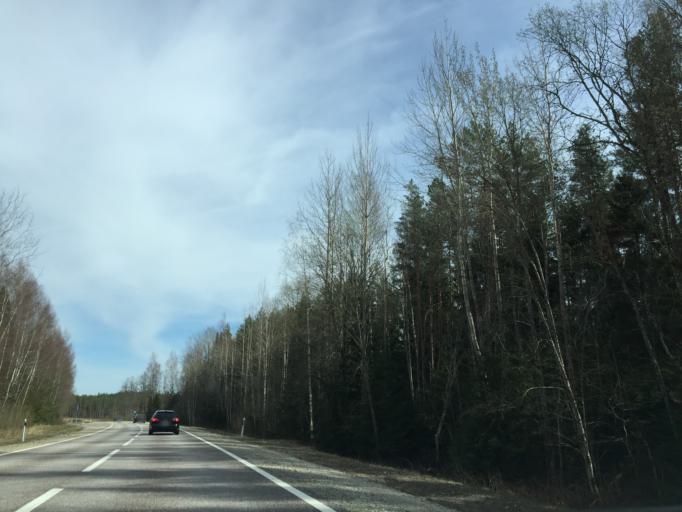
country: LV
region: Valkas Rajons
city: Valka
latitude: 57.7123
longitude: 25.9250
